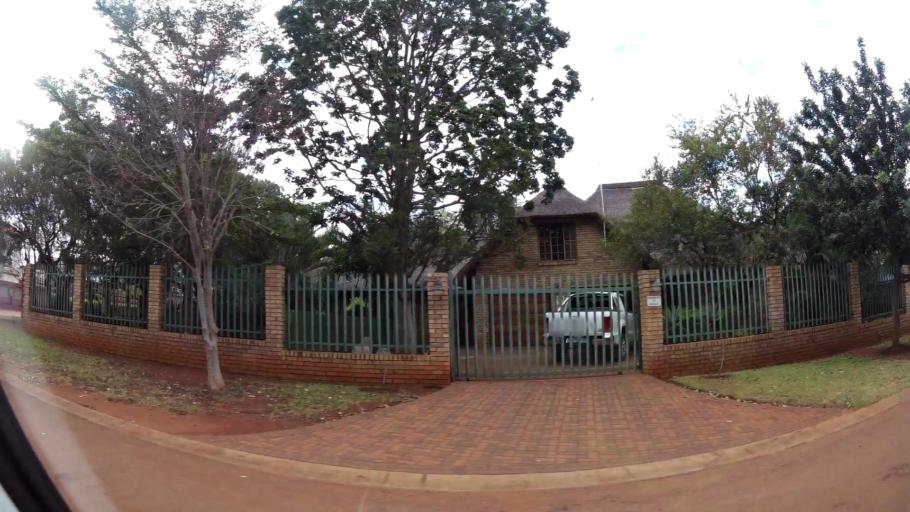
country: ZA
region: Limpopo
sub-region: Waterberg District Municipality
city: Modimolle
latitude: -24.5062
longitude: 28.7228
